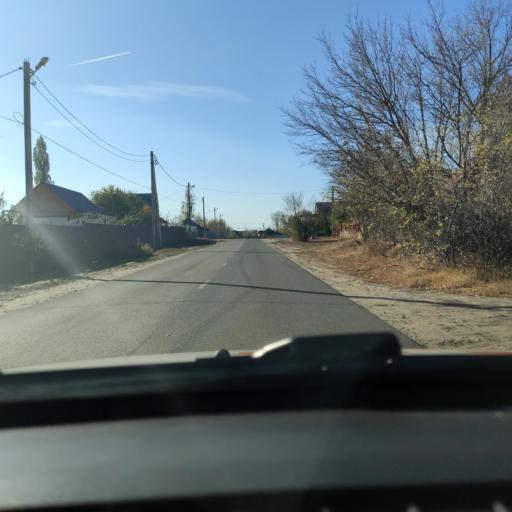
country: RU
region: Voronezj
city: Shilovo
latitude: 51.5259
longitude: 39.1508
